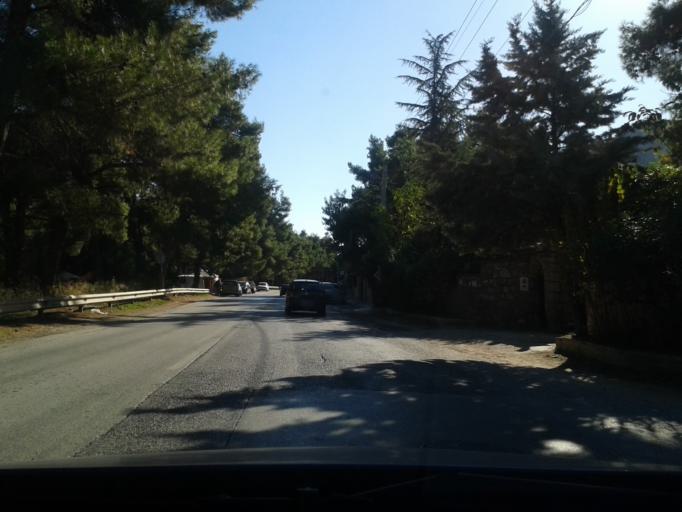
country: GR
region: Attica
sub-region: Nomarchia Anatolikis Attikis
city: Drosia
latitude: 38.1057
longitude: 23.8669
